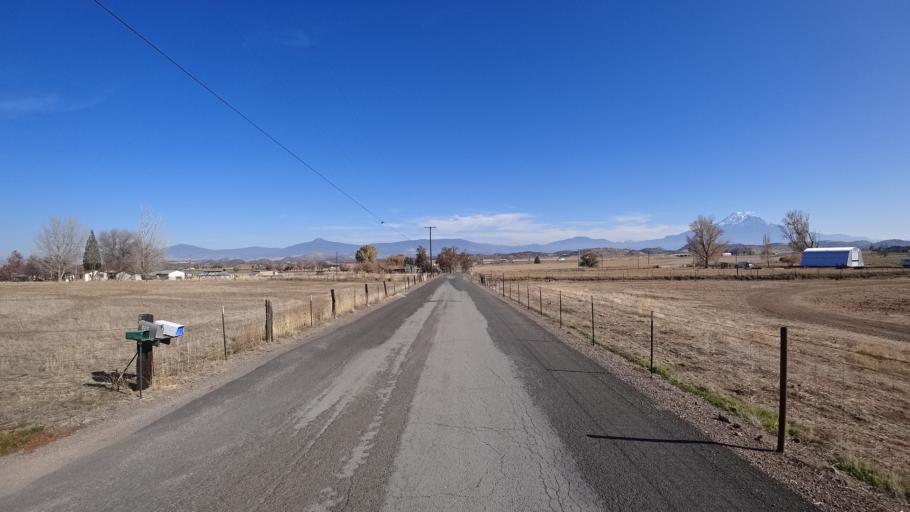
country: US
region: California
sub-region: Siskiyou County
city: Montague
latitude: 41.6327
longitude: -122.5321
